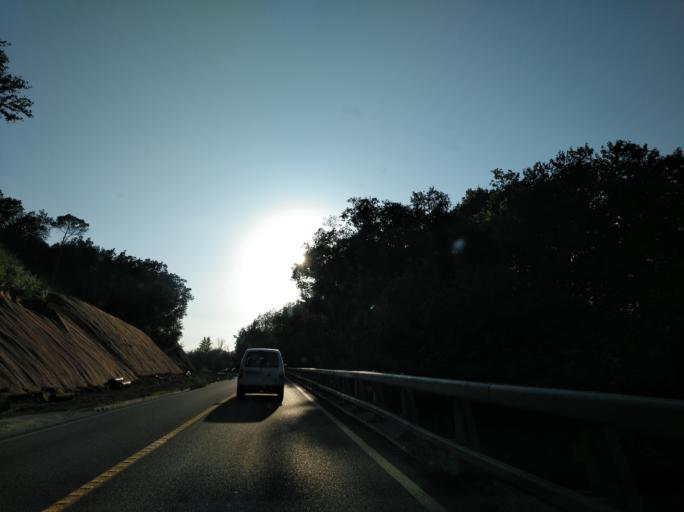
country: ES
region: Catalonia
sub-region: Provincia de Girona
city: Bescano
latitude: 41.9702
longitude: 2.7561
